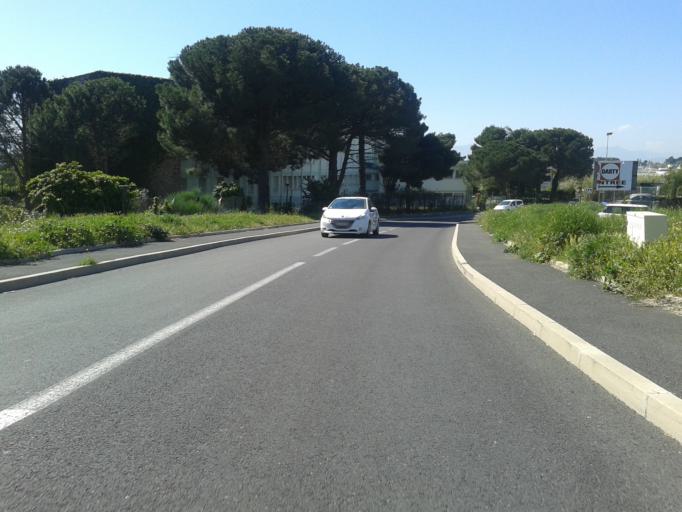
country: FR
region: Languedoc-Roussillon
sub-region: Departement des Pyrenees-Orientales
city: Perpignan
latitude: 42.6809
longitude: 2.8958
